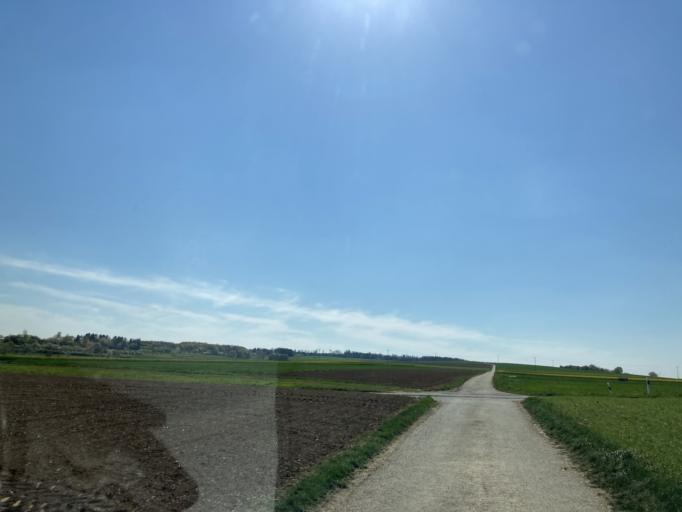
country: DE
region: Baden-Wuerttemberg
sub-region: Tuebingen Region
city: Rottenburg
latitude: 48.5344
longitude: 8.9200
